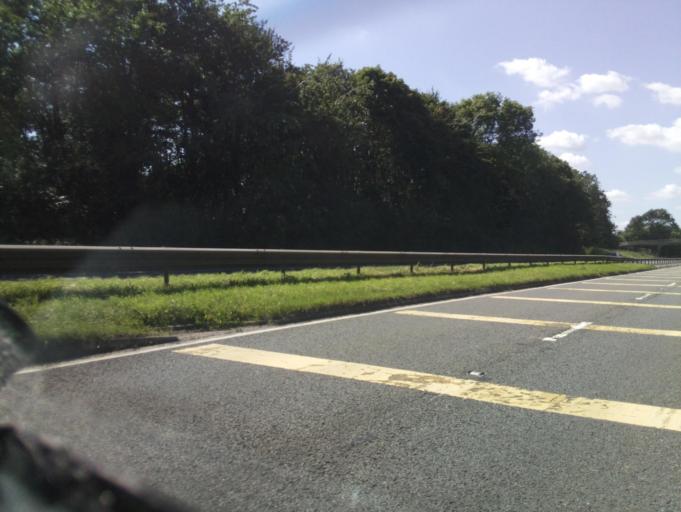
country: GB
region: England
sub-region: Warwickshire
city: Atherstone
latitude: 52.5742
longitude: -1.5300
